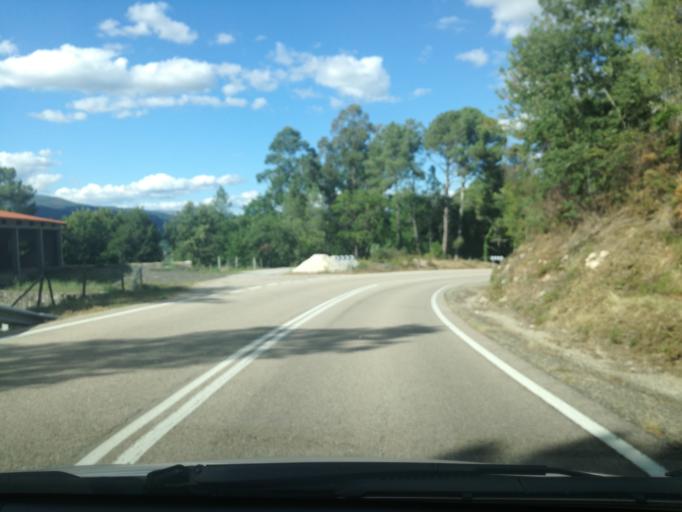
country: ES
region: Galicia
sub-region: Provincia de Ourense
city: Lobios
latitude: 41.8938
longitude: -8.0874
